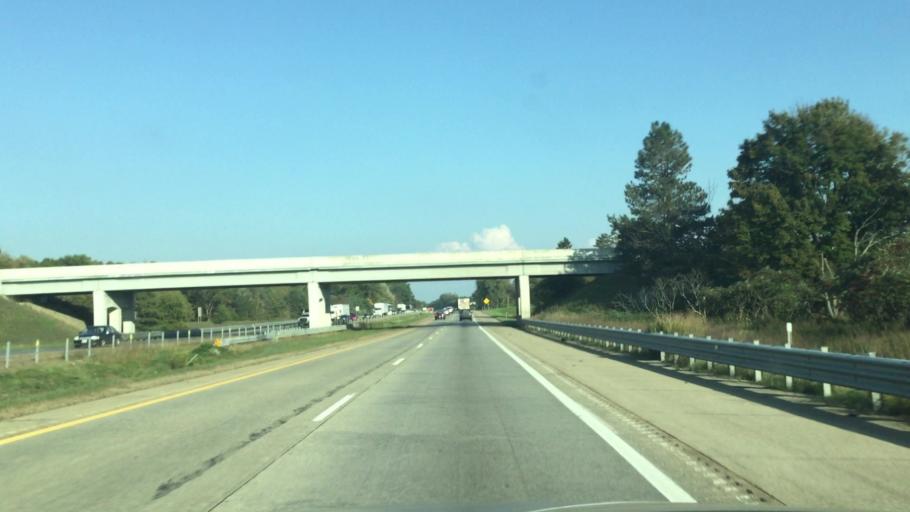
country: US
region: Michigan
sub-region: Jackson County
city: Grass Lake
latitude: 42.2962
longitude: -84.1469
